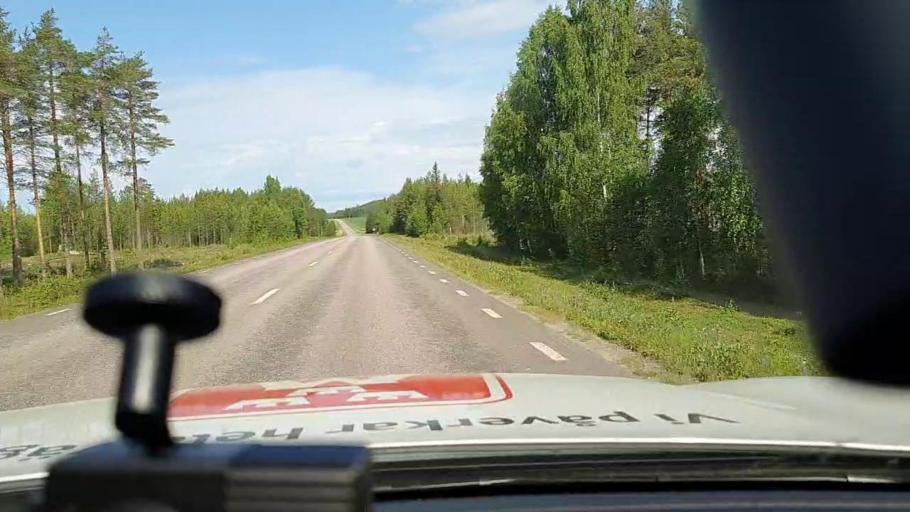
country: SE
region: Norrbotten
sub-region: Bodens Kommun
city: Boden
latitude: 65.9078
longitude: 21.3573
